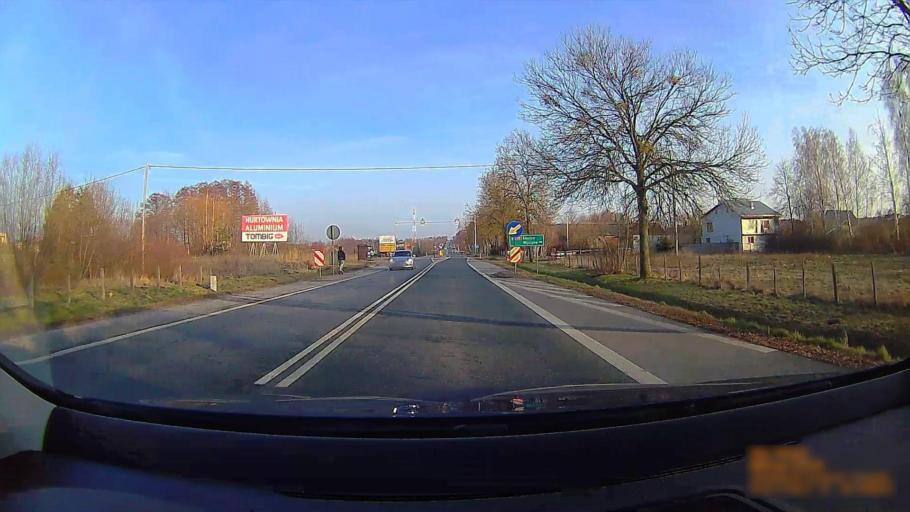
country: PL
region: Greater Poland Voivodeship
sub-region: Konin
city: Konin
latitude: 52.1910
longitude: 18.3310
